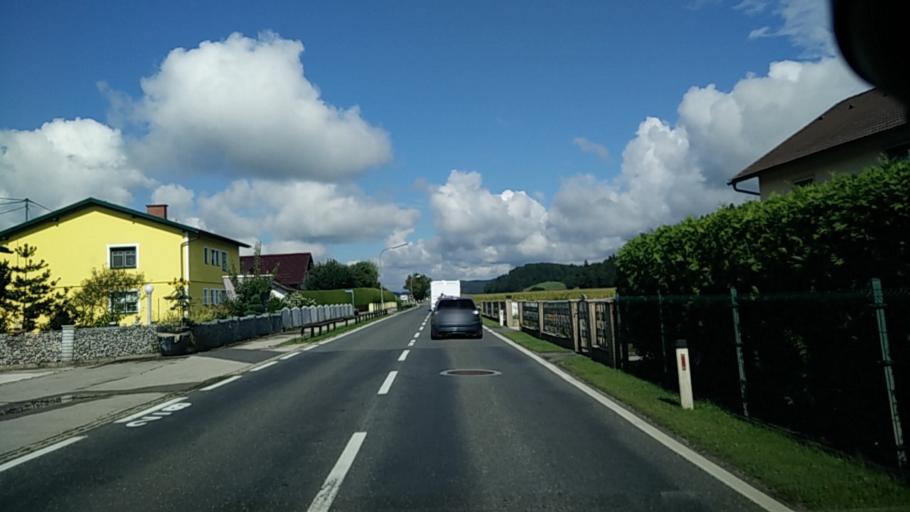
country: AT
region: Carinthia
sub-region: Politischer Bezirk Klagenfurt Land
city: Grafenstein
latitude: 46.6343
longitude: 14.5346
